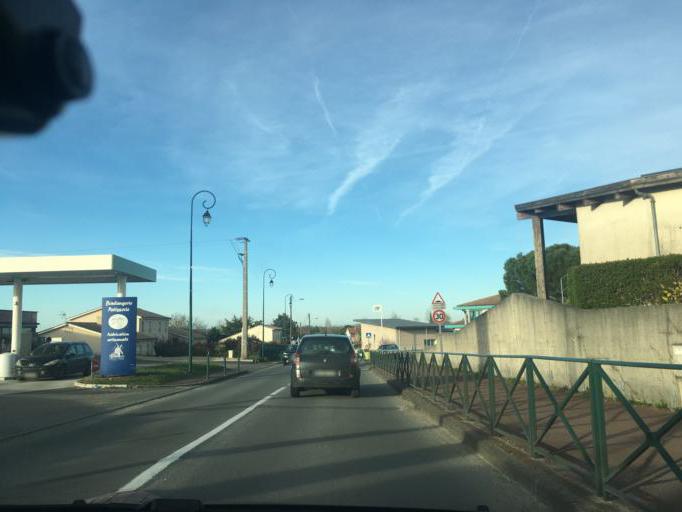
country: FR
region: Aquitaine
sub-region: Departement de la Gironde
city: Saint-Germain-du-Puch
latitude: 44.8577
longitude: -0.3223
